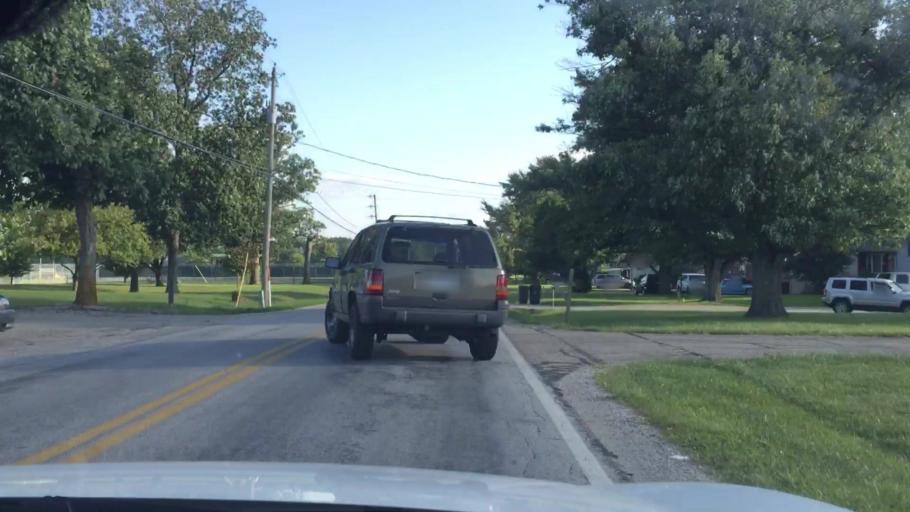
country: US
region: Ohio
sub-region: Clark County
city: Lisbon
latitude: 39.9409
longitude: -83.6820
